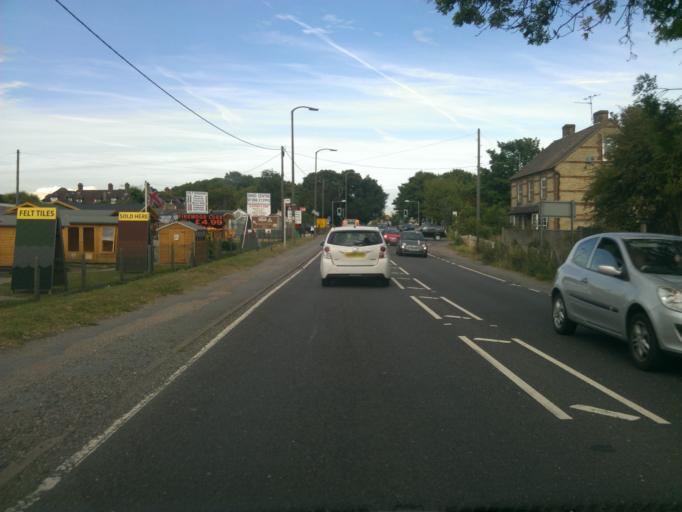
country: GB
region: England
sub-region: Essex
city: Marks Tey
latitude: 51.8789
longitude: 0.7779
